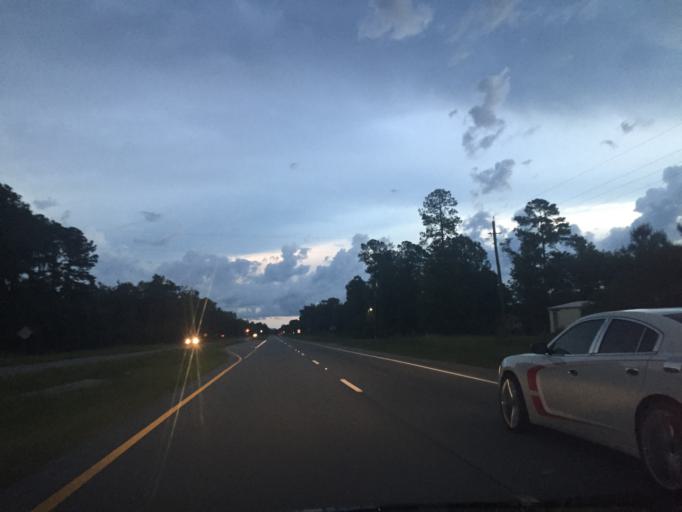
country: US
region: Georgia
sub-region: Liberty County
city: Hinesville
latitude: 31.8263
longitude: -81.5152
